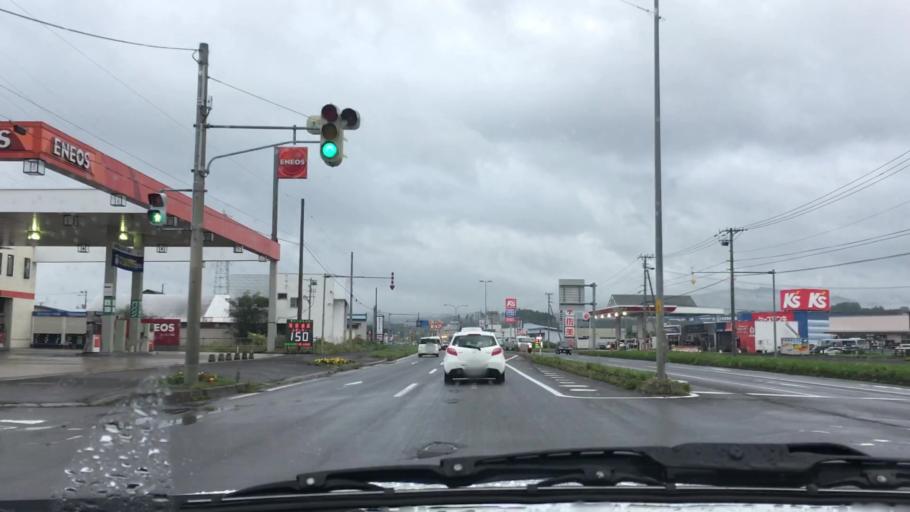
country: JP
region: Hokkaido
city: Nanae
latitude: 42.2514
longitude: 140.2850
